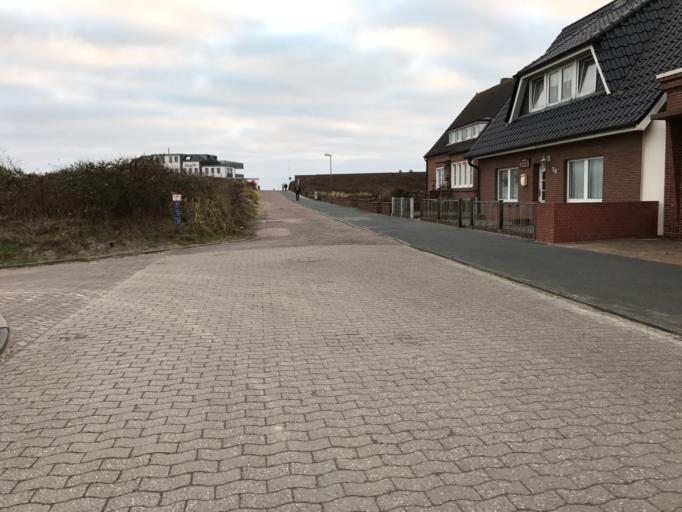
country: DE
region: Lower Saxony
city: Borkum
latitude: 53.5817
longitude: 6.6633
